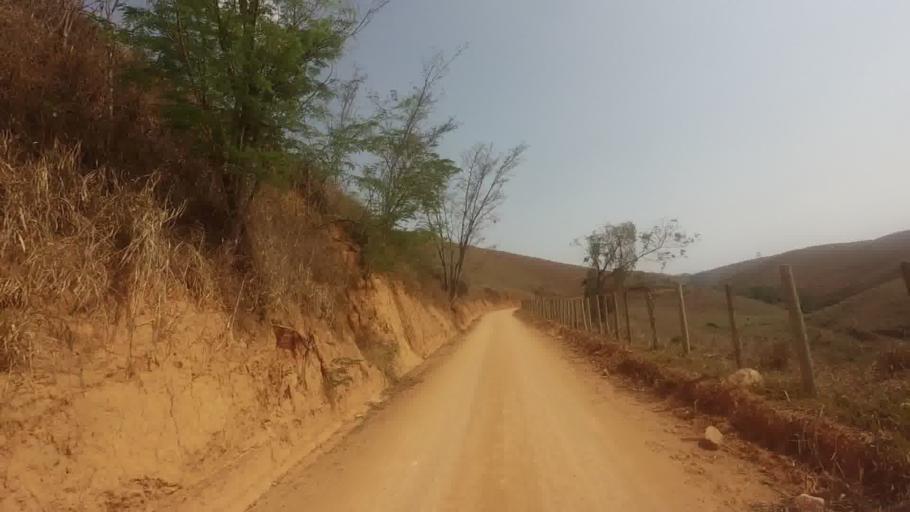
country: BR
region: Espirito Santo
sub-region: Sao Jose Do Calcado
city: Sao Jose do Calcado
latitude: -21.0620
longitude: -41.5414
